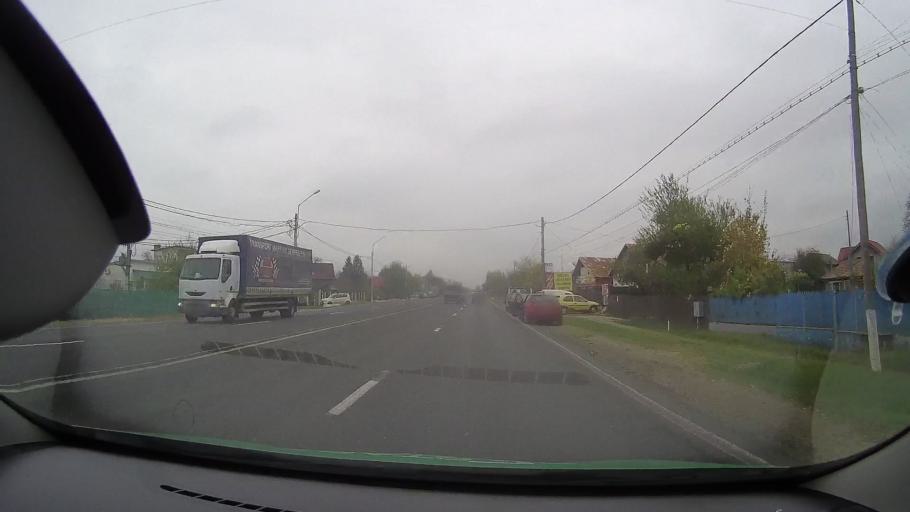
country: RO
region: Ilfov
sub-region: Comuna Ciolpani
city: Ciolpani
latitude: 44.6850
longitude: 26.0788
